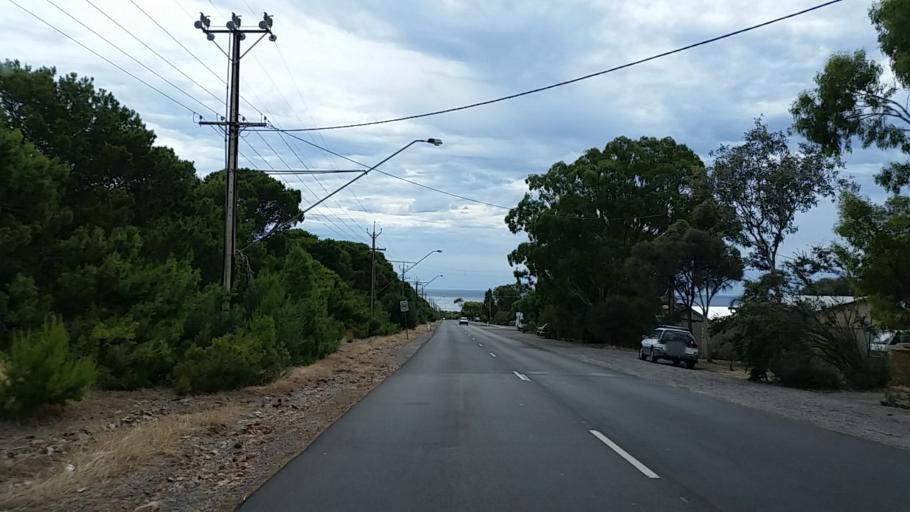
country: AU
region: South Australia
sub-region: Onkaparinga
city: Aldinga
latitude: -35.3289
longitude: 138.4610
